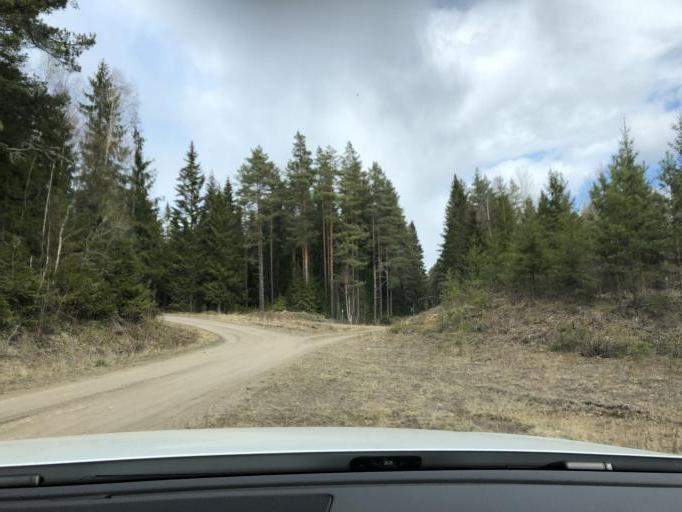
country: SE
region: Gaevleborg
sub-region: Gavle Kommun
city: Hedesunda
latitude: 60.3362
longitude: 17.1100
